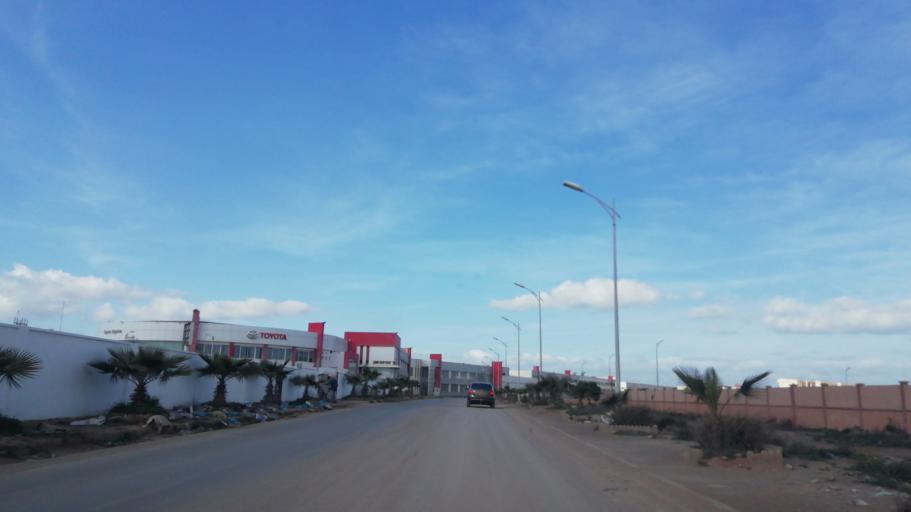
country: DZ
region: Oran
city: Es Senia
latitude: 35.6363
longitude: -0.5860
